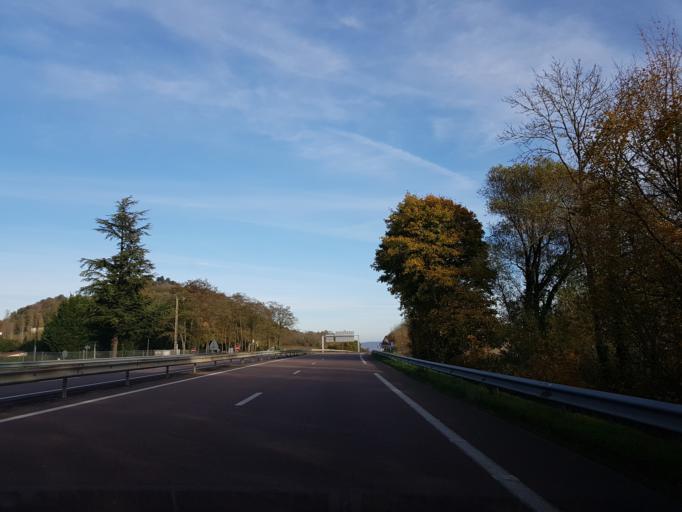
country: FR
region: Bourgogne
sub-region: Departement de la Cote-d'Or
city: Fleurey-sur-Ouche
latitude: 47.3078
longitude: 4.7350
